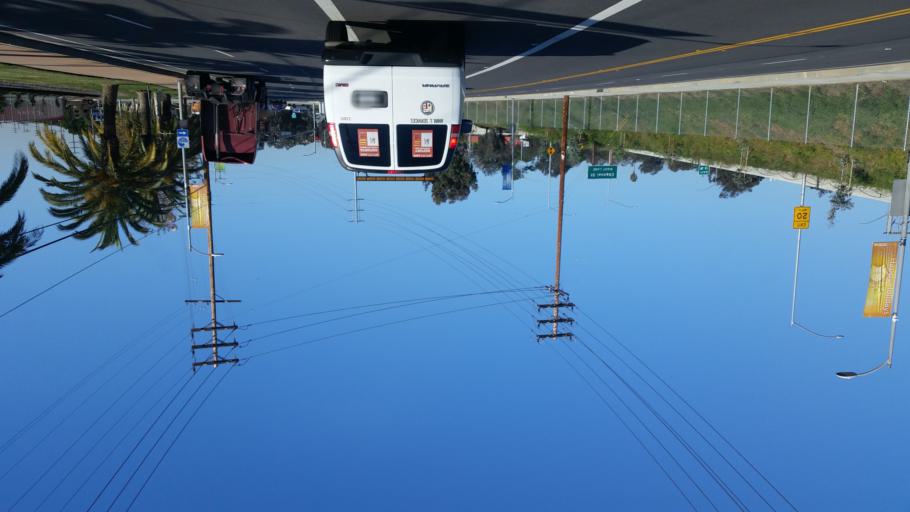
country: US
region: California
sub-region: Los Angeles County
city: San Pedro
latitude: 33.7550
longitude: -118.2905
